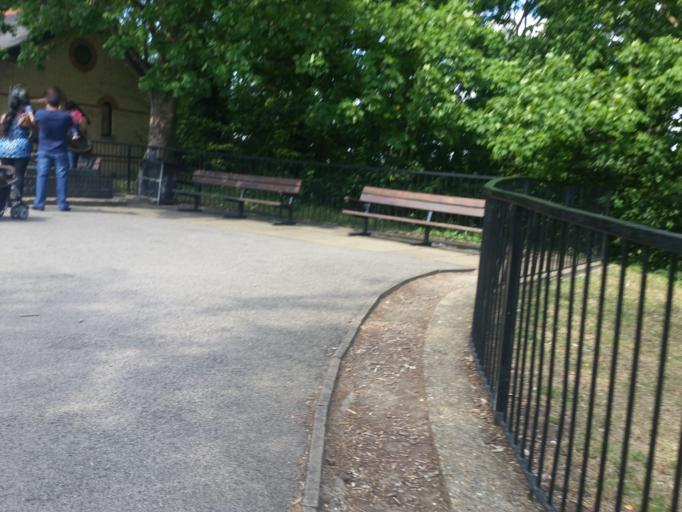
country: GB
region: England
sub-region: Greater London
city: Wood Green
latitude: 51.5964
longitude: -0.1303
